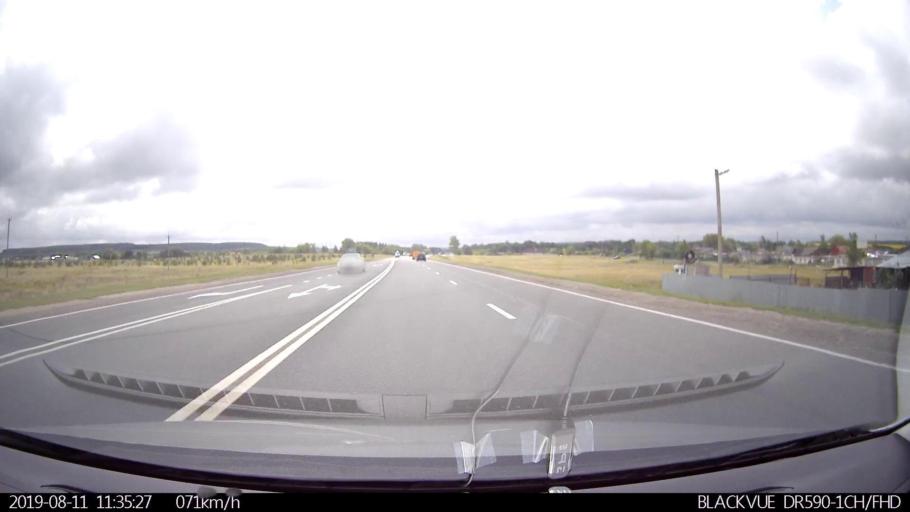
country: RU
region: Ulyanovsk
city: Silikatnyy
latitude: 54.0059
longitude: 48.2198
